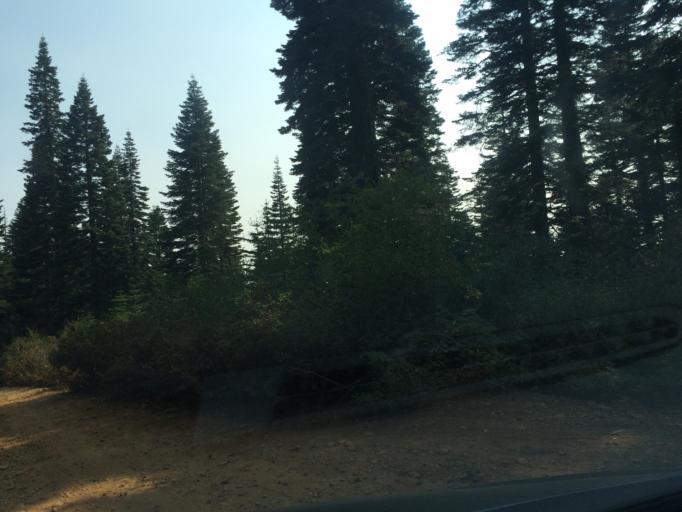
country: US
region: California
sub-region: Sierra County
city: Downieville
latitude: 39.3936
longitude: -120.6618
